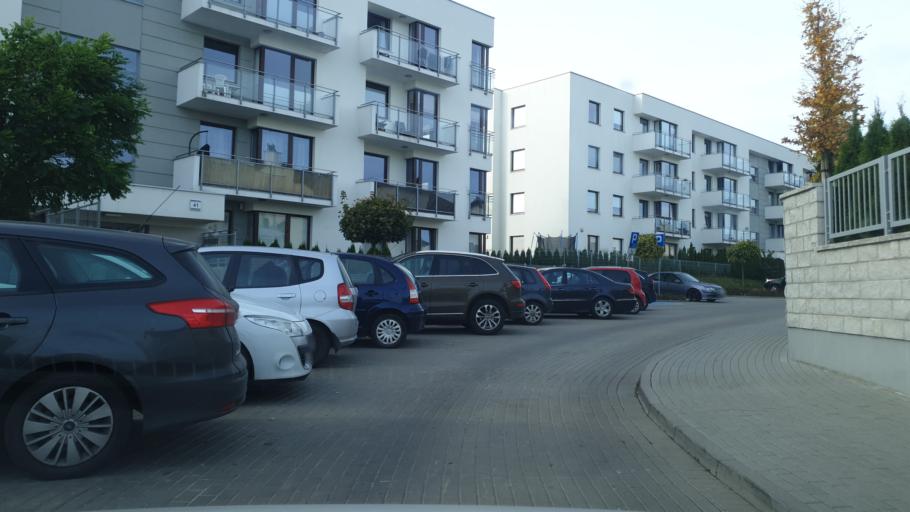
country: PL
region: Pomeranian Voivodeship
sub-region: Powiat gdanski
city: Kowale
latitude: 54.3466
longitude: 18.5904
